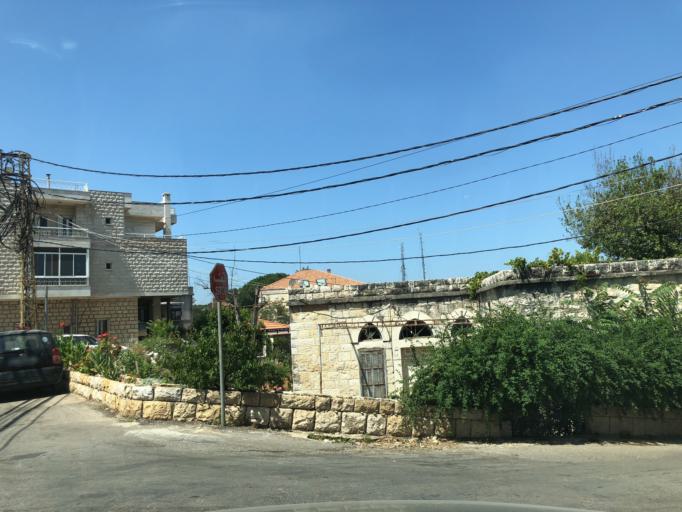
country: LB
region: Mont-Liban
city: Jdaidet el Matn
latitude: 33.8672
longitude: 35.6049
